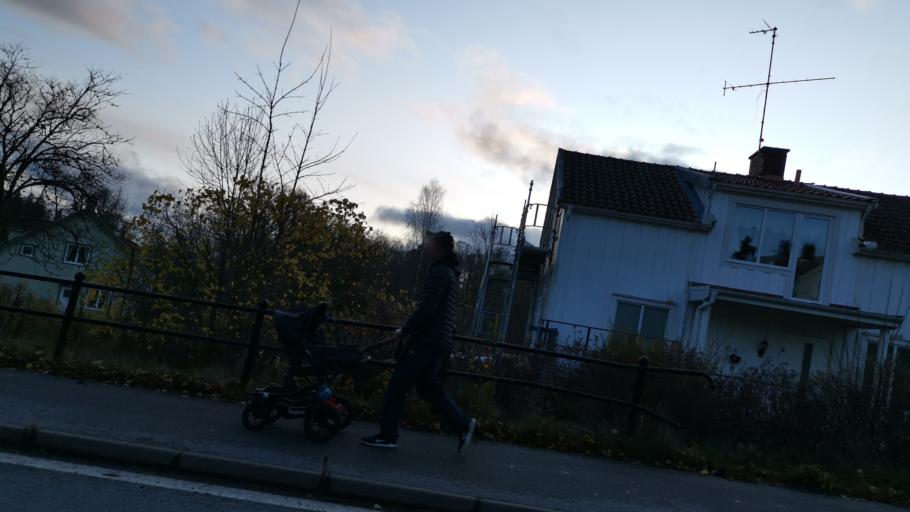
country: SE
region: Vaestra Goetaland
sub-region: Munkedals Kommun
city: Munkedal
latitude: 58.4855
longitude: 11.6959
